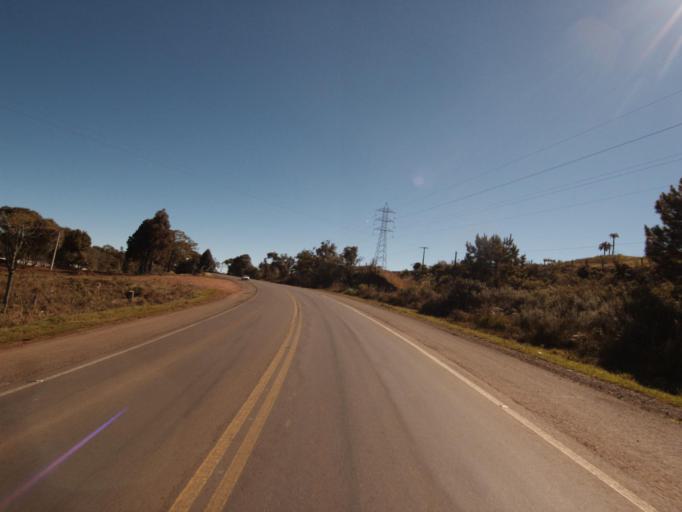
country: BR
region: Santa Catarina
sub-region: Concordia
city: Concordia
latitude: -26.8937
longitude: -51.9802
